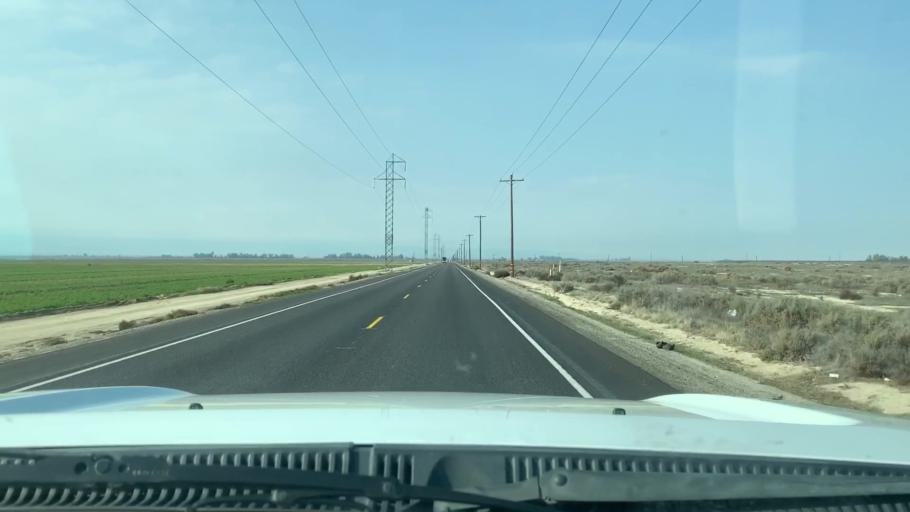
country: US
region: California
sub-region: Kern County
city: Shafter
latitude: 35.4421
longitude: -119.3590
